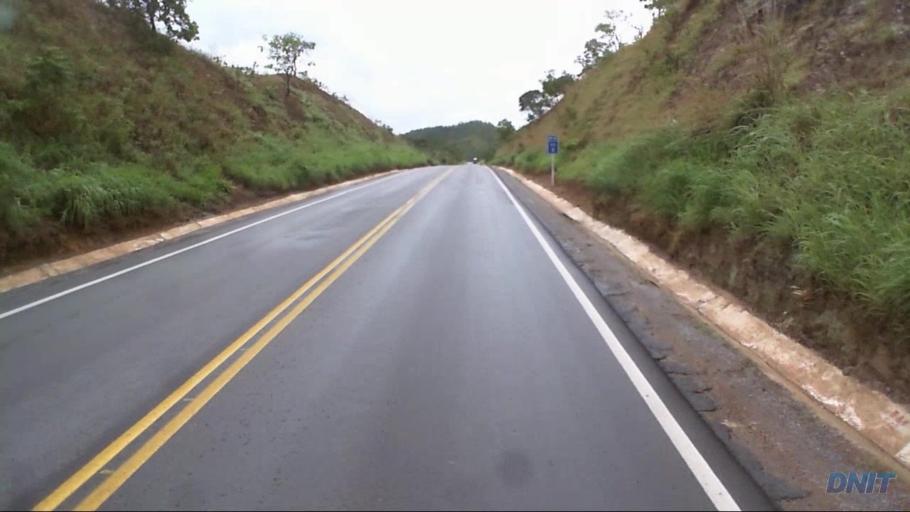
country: BR
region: Goias
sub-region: Padre Bernardo
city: Padre Bernardo
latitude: -15.4876
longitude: -48.2318
